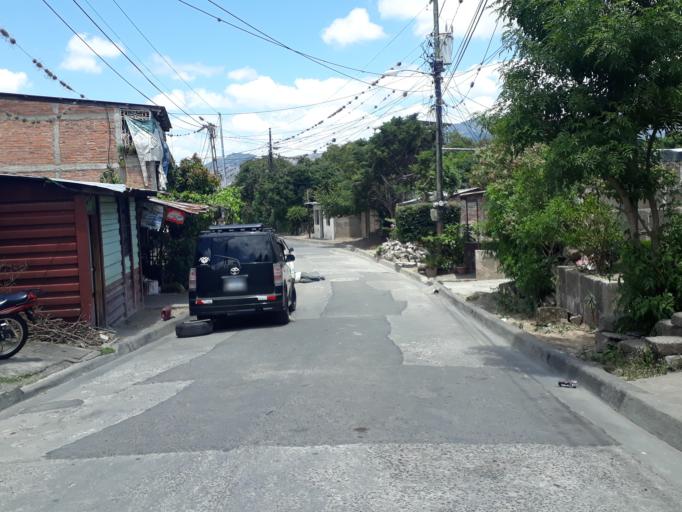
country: NI
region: Matagalpa
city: Matagalpa
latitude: 12.9205
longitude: -85.9141
